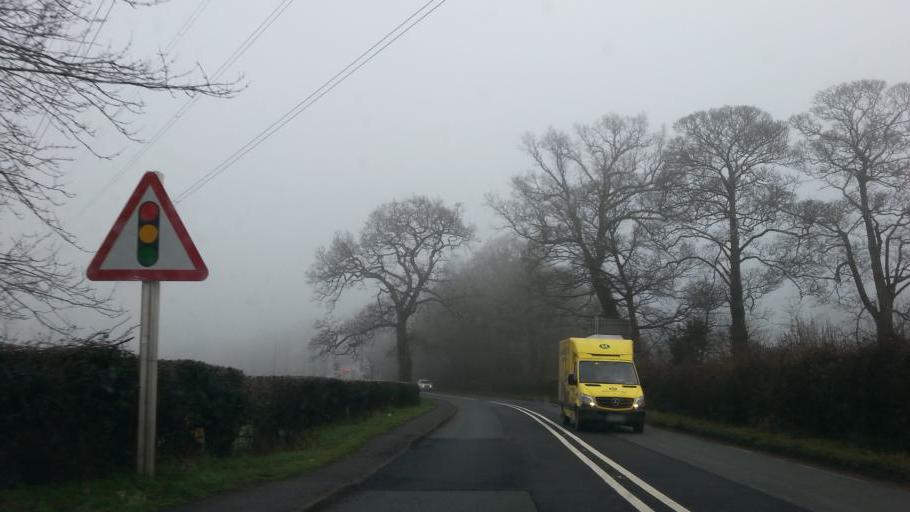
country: GB
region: England
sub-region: Cheshire East
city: Siddington
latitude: 53.2657
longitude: -2.2346
